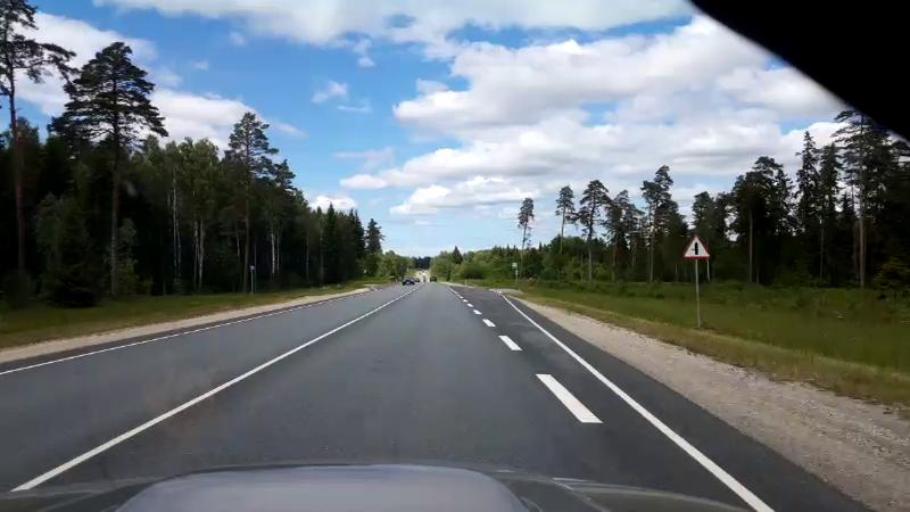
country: EE
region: Raplamaa
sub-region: Maerjamaa vald
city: Marjamaa
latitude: 59.0232
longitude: 24.4494
